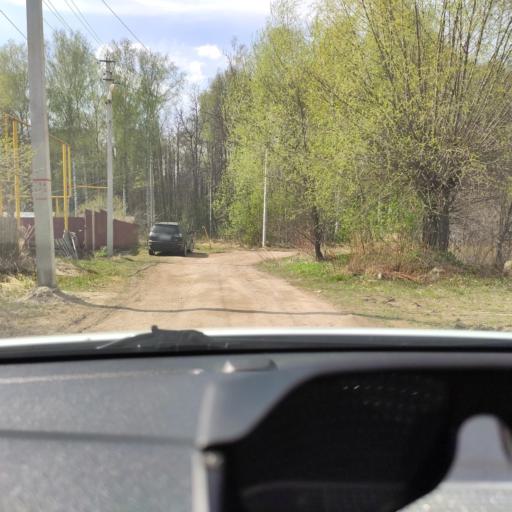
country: RU
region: Tatarstan
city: Vysokaya Gora
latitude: 55.9338
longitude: 49.2986
